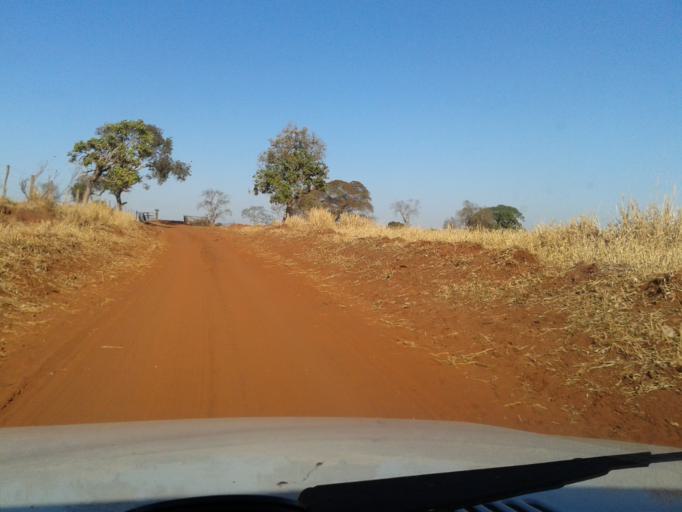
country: BR
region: Minas Gerais
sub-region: Santa Vitoria
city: Santa Vitoria
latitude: -18.9910
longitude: -49.9046
